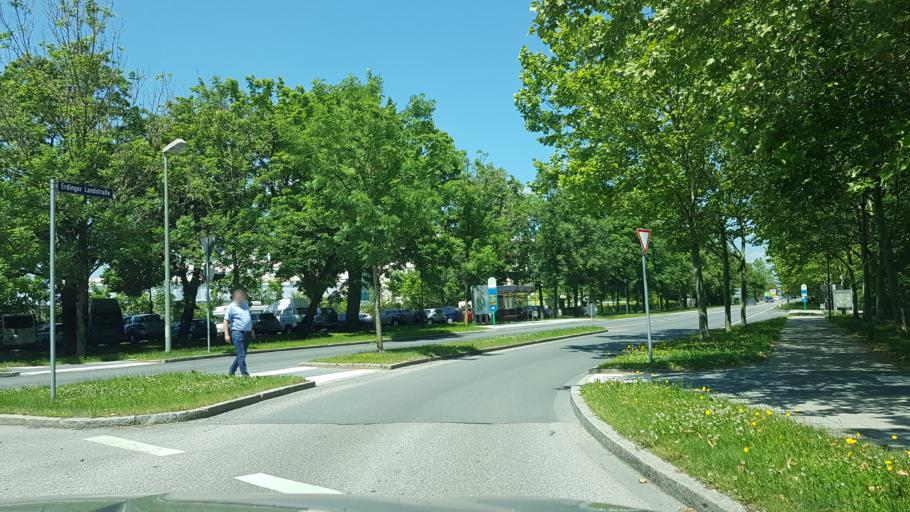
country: DE
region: Bavaria
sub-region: Upper Bavaria
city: Aschheim
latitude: 48.1475
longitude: 11.6855
